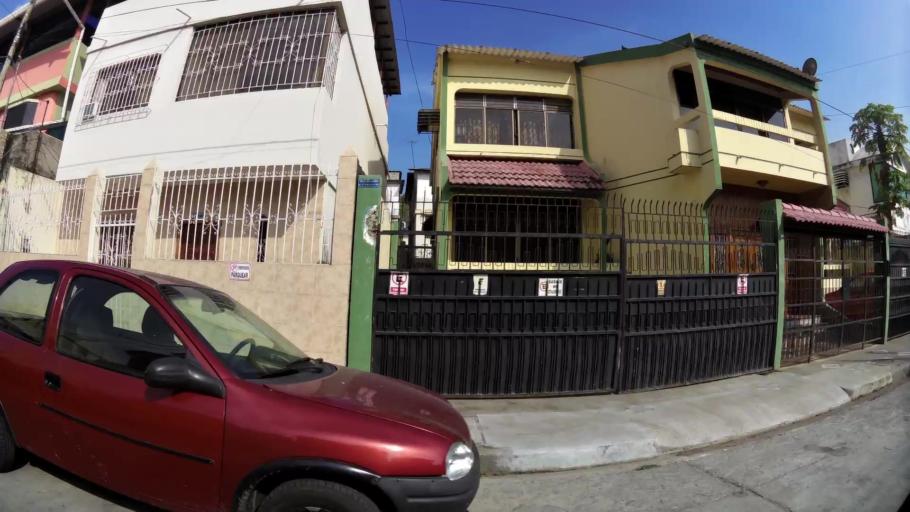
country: EC
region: Guayas
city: Guayaquil
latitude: -2.1855
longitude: -79.9105
